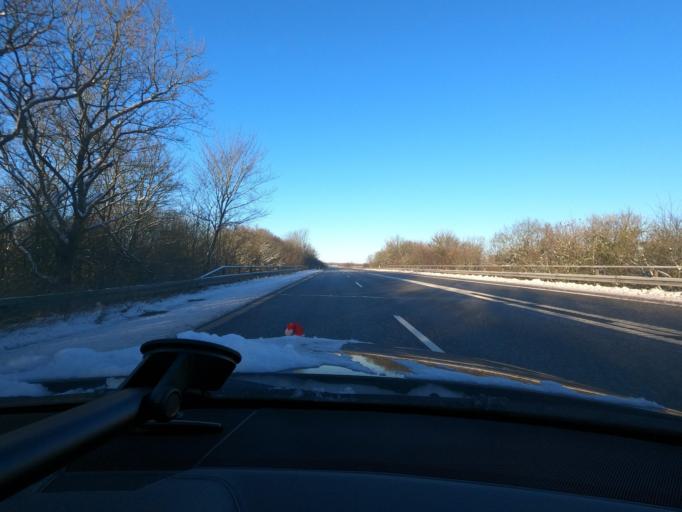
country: DK
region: South Denmark
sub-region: Aabenraa Kommune
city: Aabenraa
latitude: 55.0257
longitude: 9.3607
